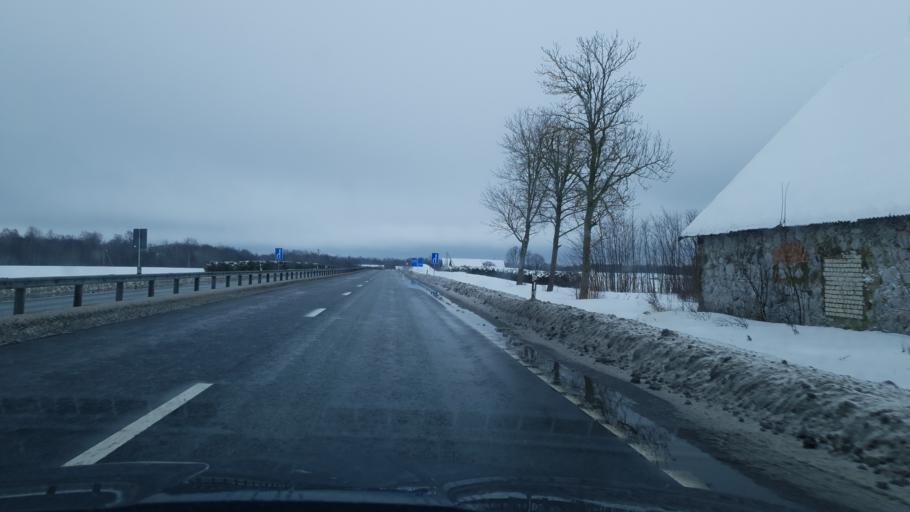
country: EE
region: Jogevamaa
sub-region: Poltsamaa linn
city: Poltsamaa
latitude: 58.6404
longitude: 26.0784
